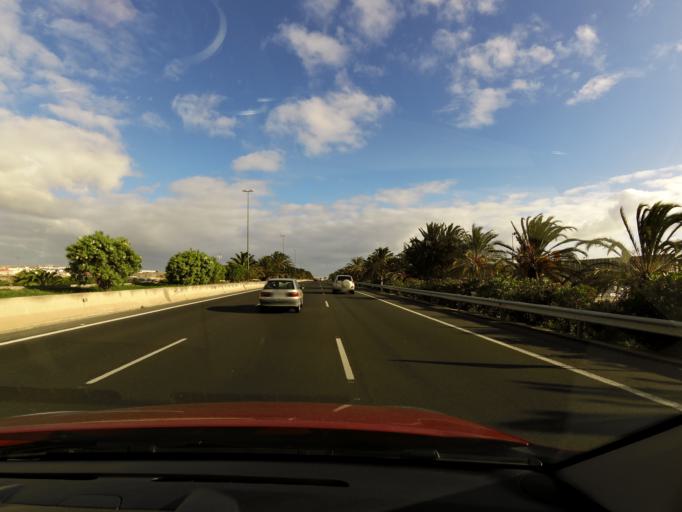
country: ES
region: Canary Islands
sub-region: Provincia de Las Palmas
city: Ingenio
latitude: 27.9373
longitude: -15.3920
